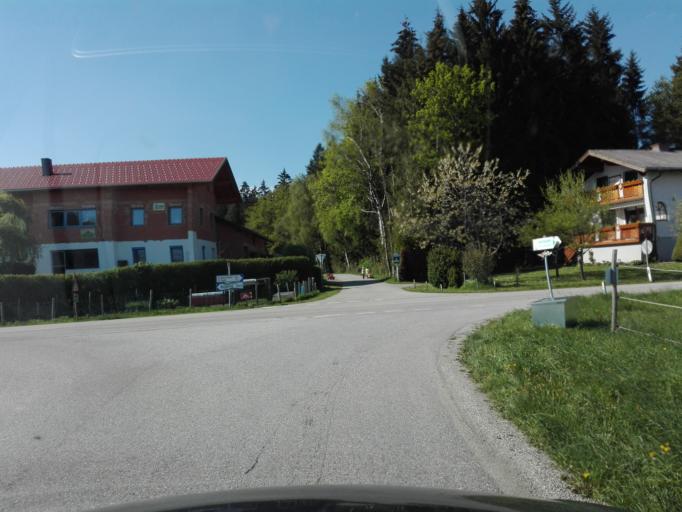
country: DE
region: Bavaria
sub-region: Lower Bavaria
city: Obernzell
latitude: 48.4471
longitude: 13.6838
